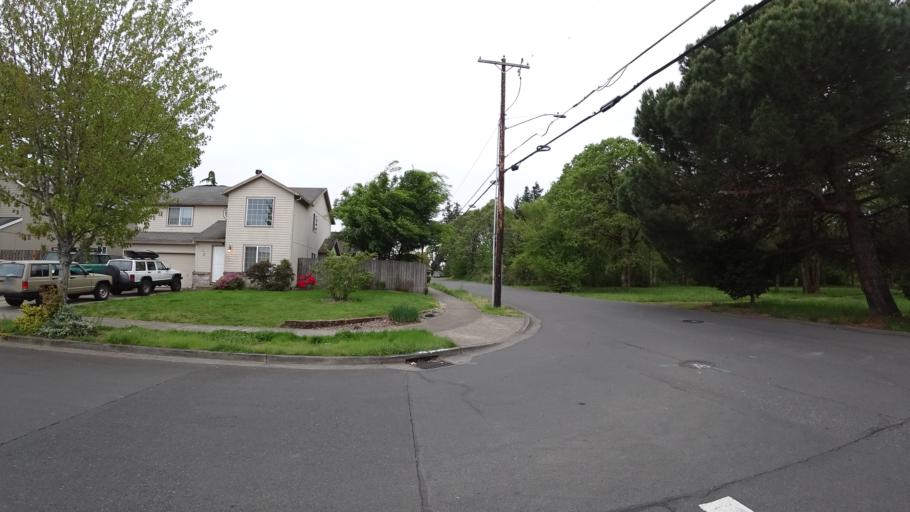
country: US
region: Oregon
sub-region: Washington County
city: Aloha
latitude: 45.5143
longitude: -122.9145
